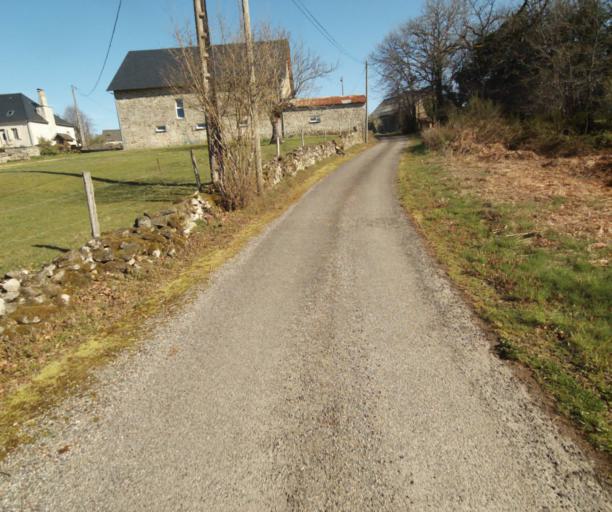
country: FR
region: Limousin
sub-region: Departement de la Correze
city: Correze
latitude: 45.2703
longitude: 1.9206
